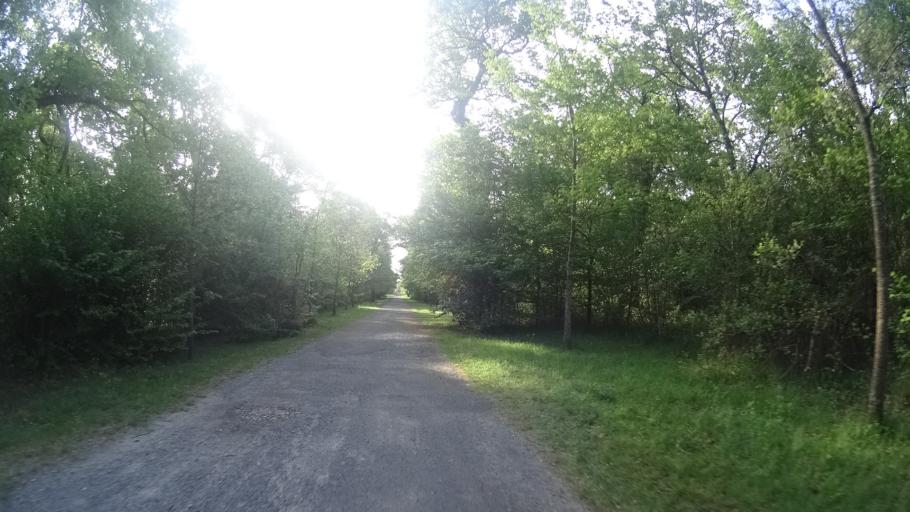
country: FR
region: Aquitaine
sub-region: Departement de la Gironde
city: Talence
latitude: 44.7901
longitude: -0.5974
